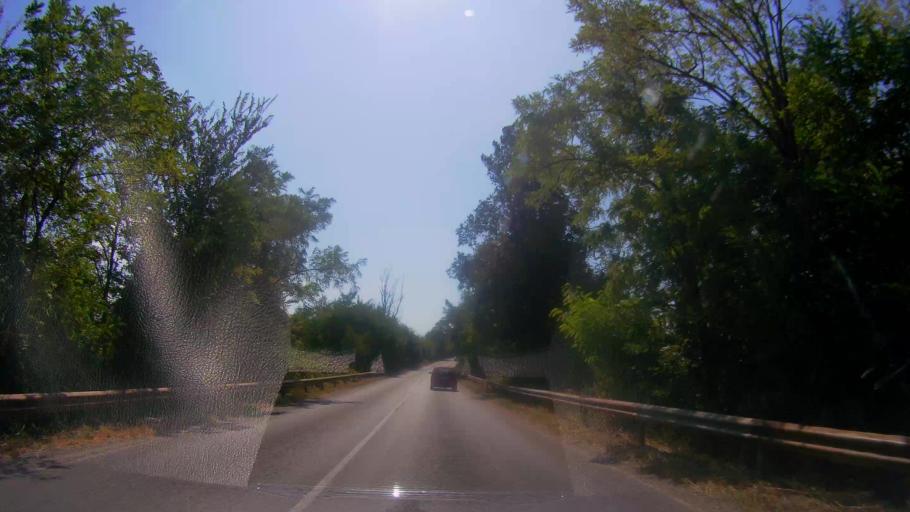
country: BG
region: Veliko Turnovo
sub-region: Obshtina Gorna Oryakhovitsa
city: Purvomaytsi
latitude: 43.2504
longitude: 25.6441
